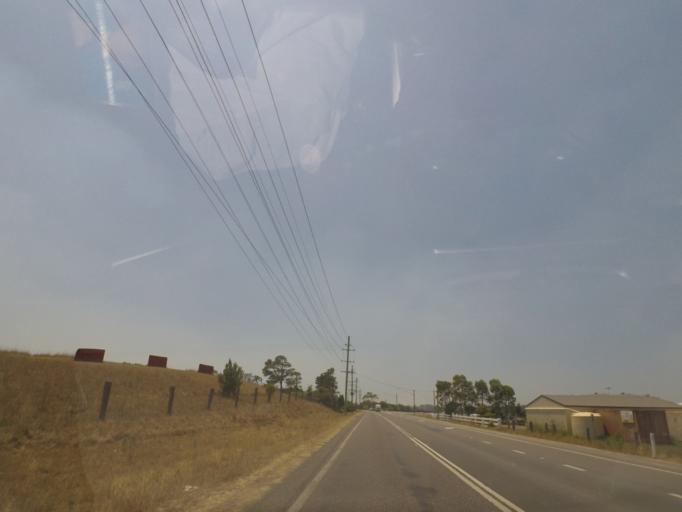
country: AU
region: New South Wales
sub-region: Port Stephens Shire
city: Medowie
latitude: -32.8028
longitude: 151.8843
